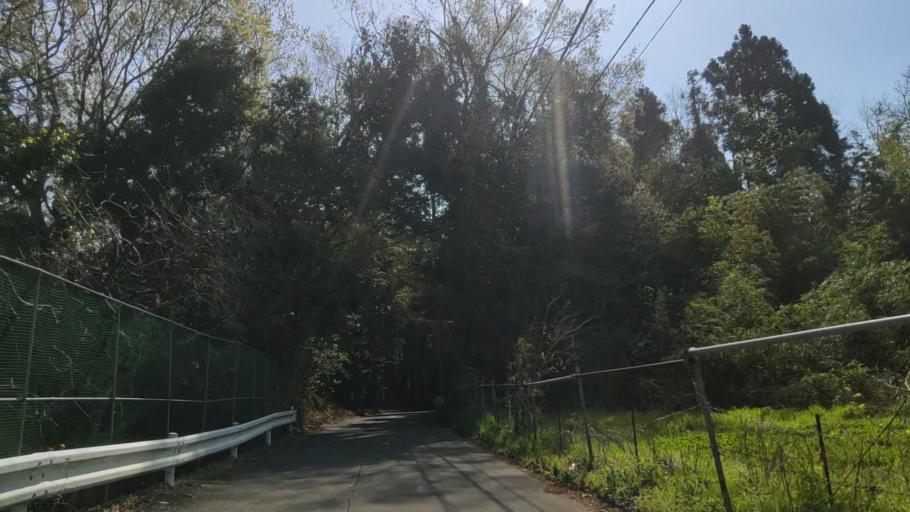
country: JP
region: Kanagawa
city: Ninomiya
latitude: 35.3267
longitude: 139.2618
